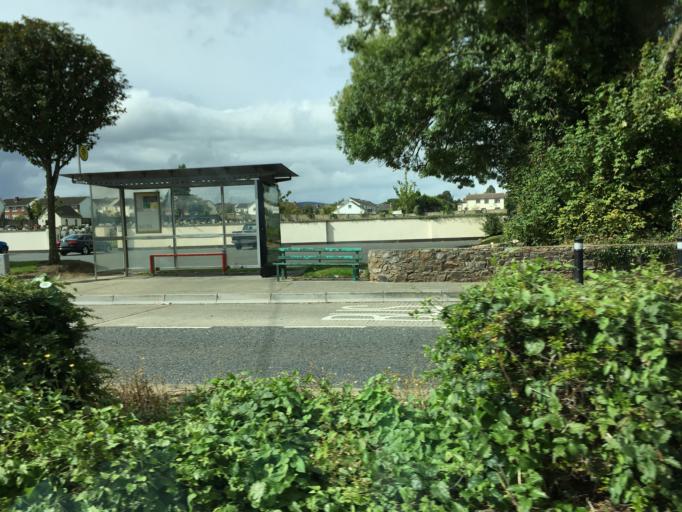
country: IE
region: Leinster
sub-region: Wicklow
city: Kilmacanoge
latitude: 53.1861
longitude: -6.1290
